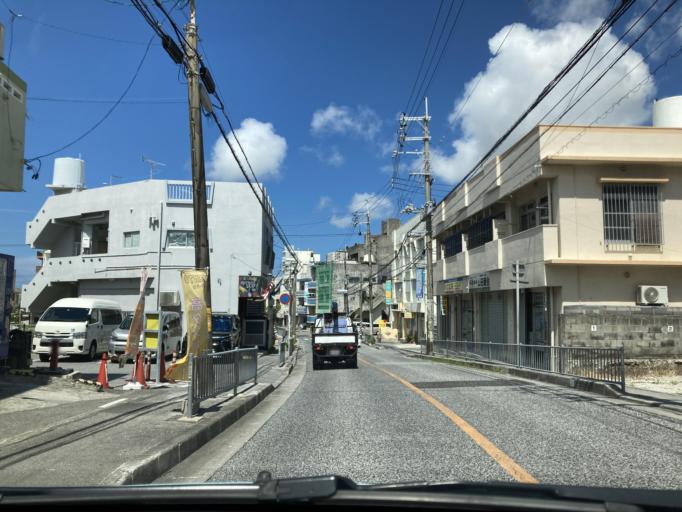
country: JP
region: Okinawa
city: Naha-shi
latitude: 26.2025
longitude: 127.7002
